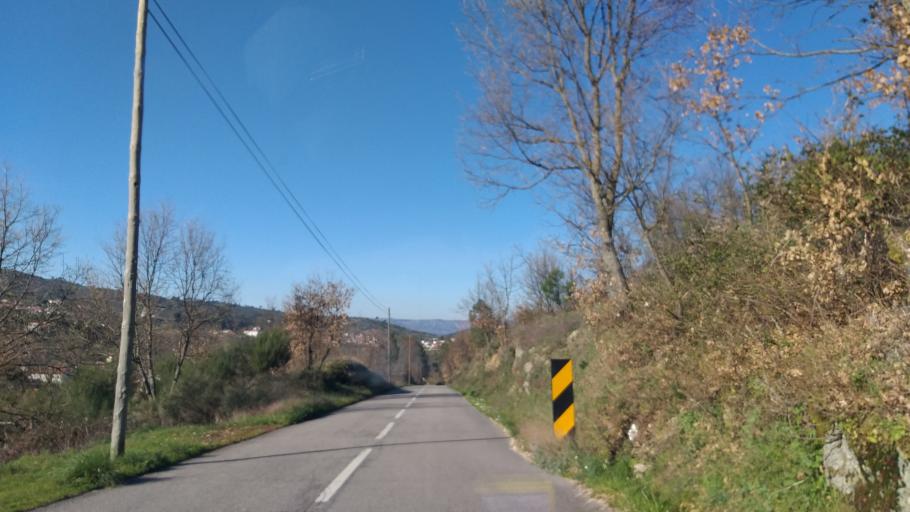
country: PT
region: Guarda
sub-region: Celorico da Beira
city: Celorico da Beira
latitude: 40.5908
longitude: -7.3623
